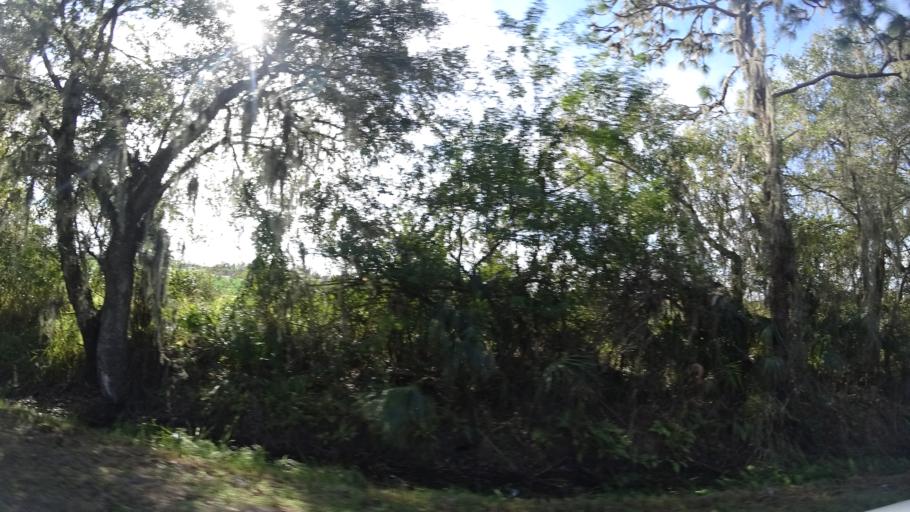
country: US
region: Florida
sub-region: Hillsborough County
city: Ruskin
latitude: 27.6305
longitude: -82.4260
